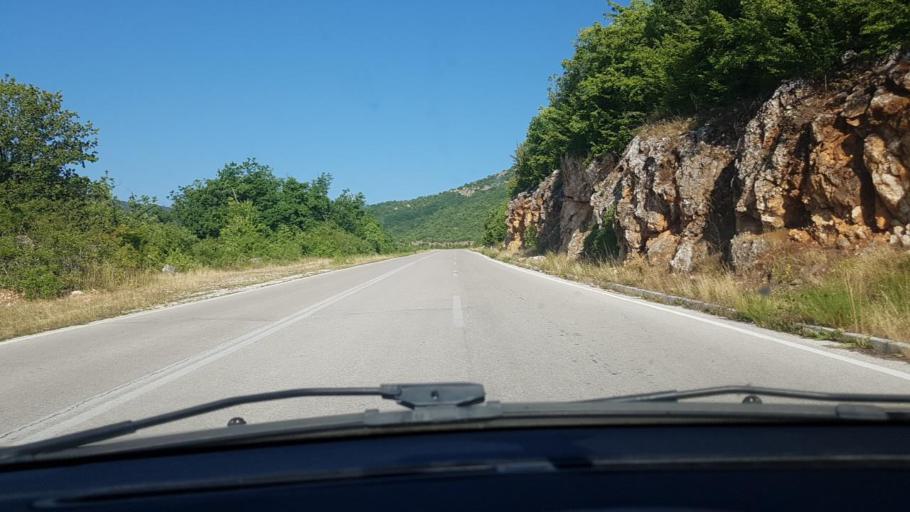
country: BA
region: Federation of Bosnia and Herzegovina
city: Rumboci
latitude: 43.8195
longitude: 17.4612
